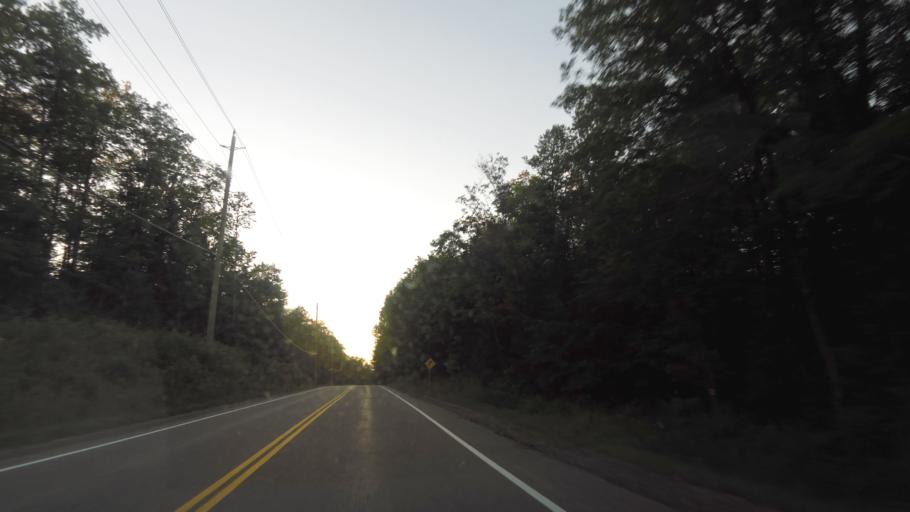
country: CA
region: Ontario
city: Bancroft
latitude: 45.0303
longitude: -78.4062
